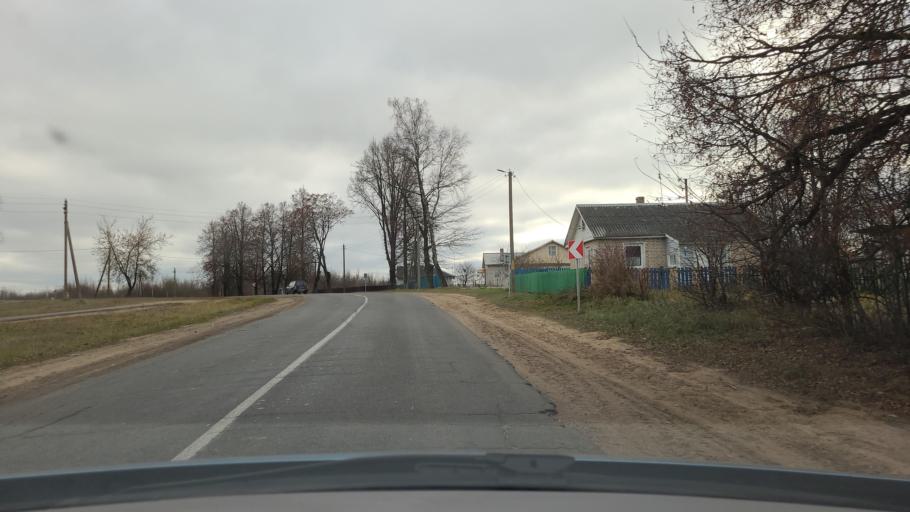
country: BY
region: Minsk
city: Krupki
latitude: 54.4000
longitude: 29.0440
